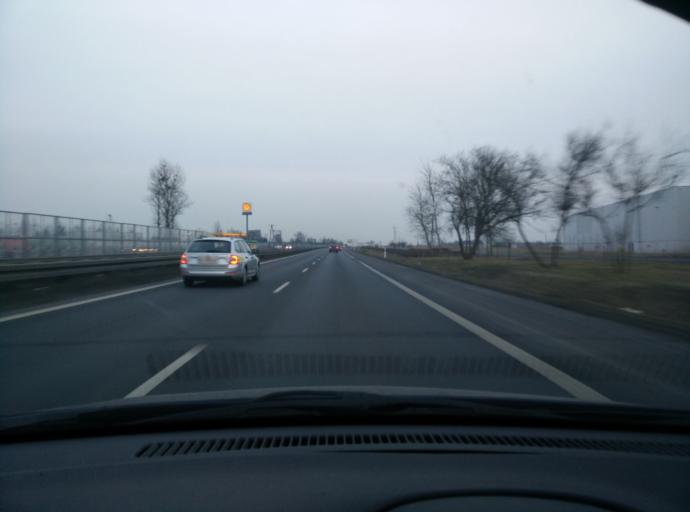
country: PL
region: Greater Poland Voivodeship
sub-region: Powiat poznanski
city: Daszewice
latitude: 52.3337
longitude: 17.0163
